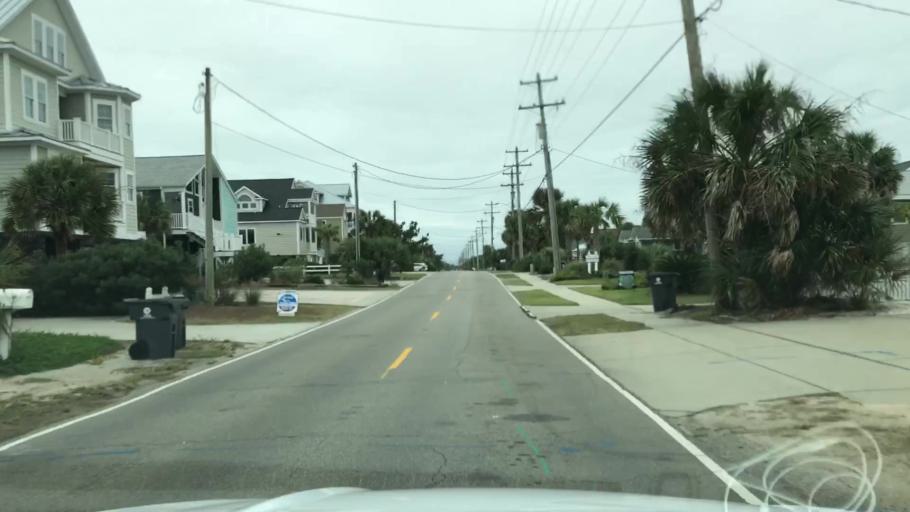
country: US
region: South Carolina
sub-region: Horry County
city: Garden City
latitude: 33.5632
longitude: -79.0106
